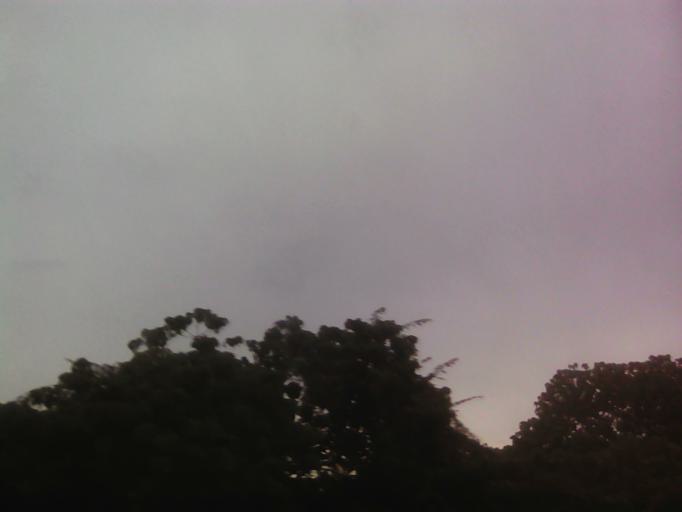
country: MY
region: Penang
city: Perai
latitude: 5.3982
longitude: 100.4127
